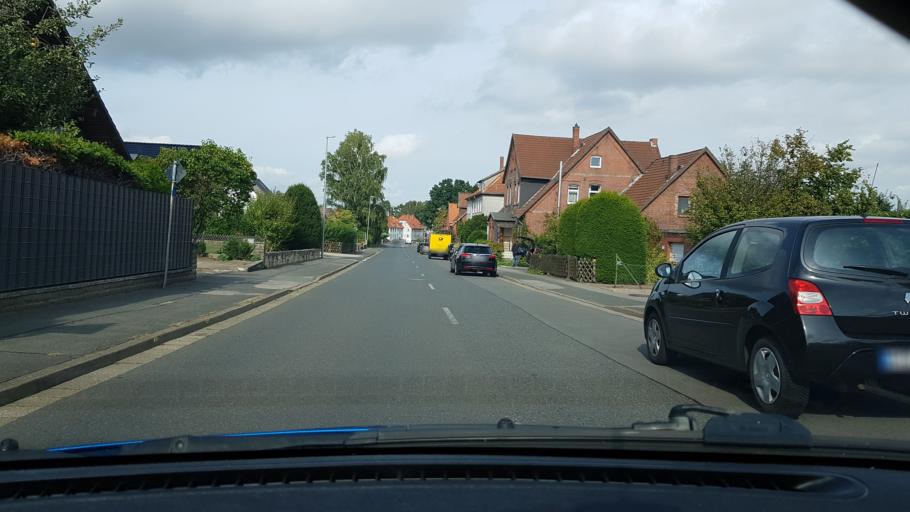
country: DE
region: Lower Saxony
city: Egestorf
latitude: 52.2941
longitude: 9.4917
